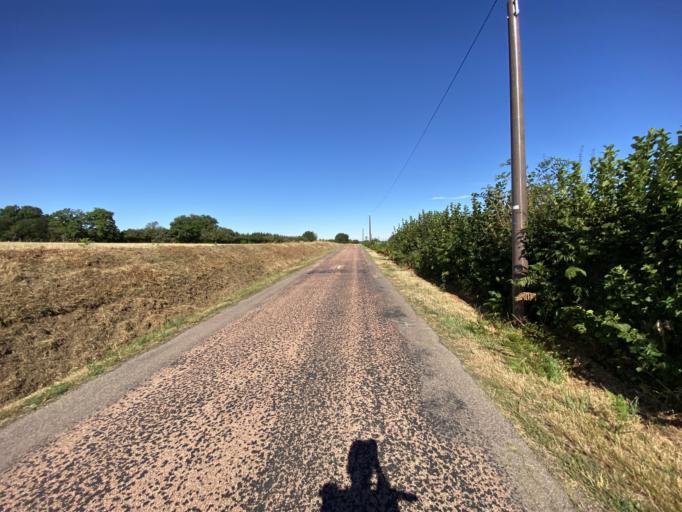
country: FR
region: Bourgogne
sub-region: Departement de la Cote-d'Or
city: Saulieu
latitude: 47.2728
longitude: 4.1644
